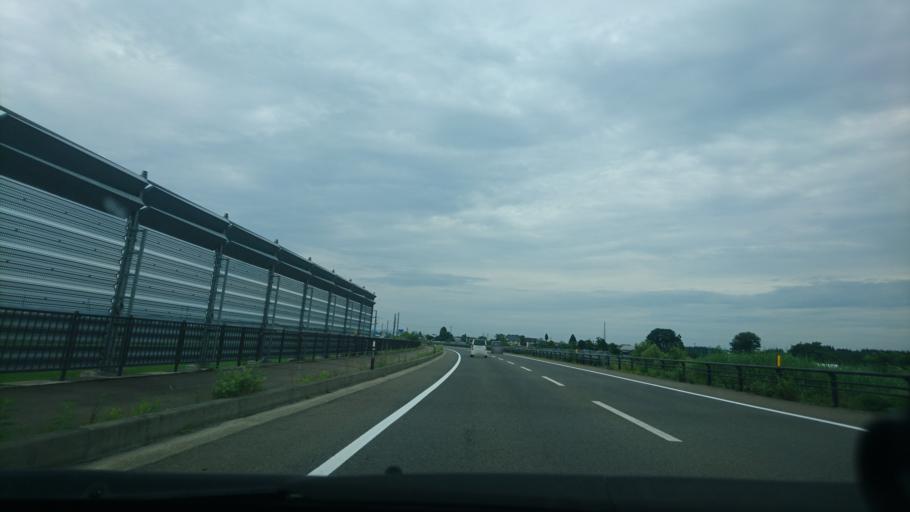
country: JP
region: Akita
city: Omagari
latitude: 39.4967
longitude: 140.4459
